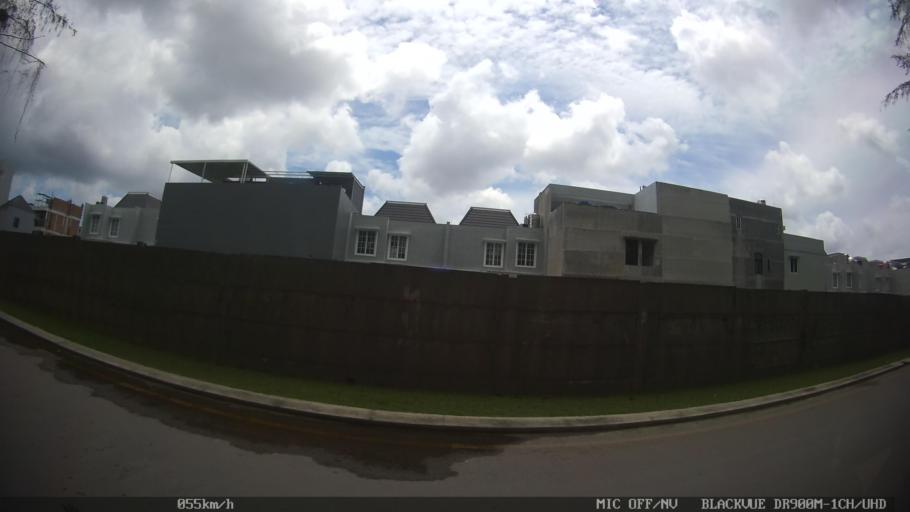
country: ID
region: North Sumatra
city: Medan
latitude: 3.6107
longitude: 98.7291
